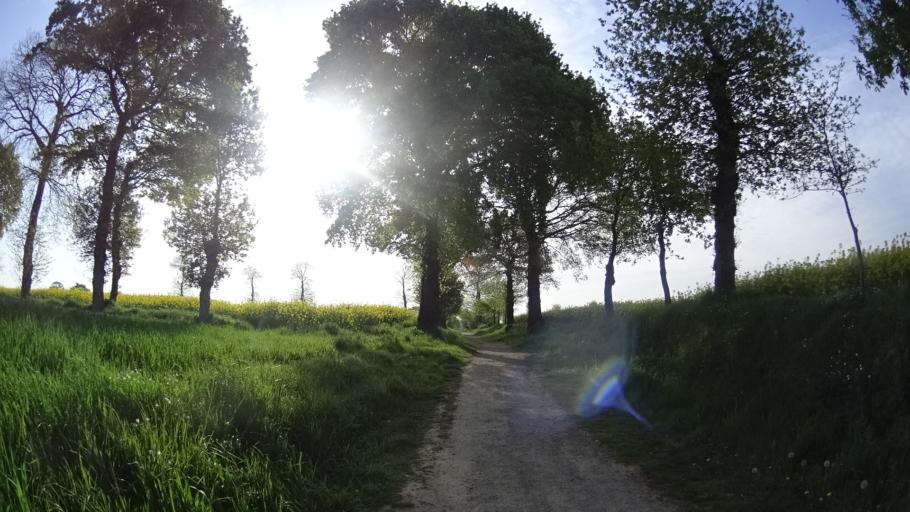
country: FR
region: Brittany
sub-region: Departement d'Ille-et-Vilaine
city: La Meziere
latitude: 48.2202
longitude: -1.7706
